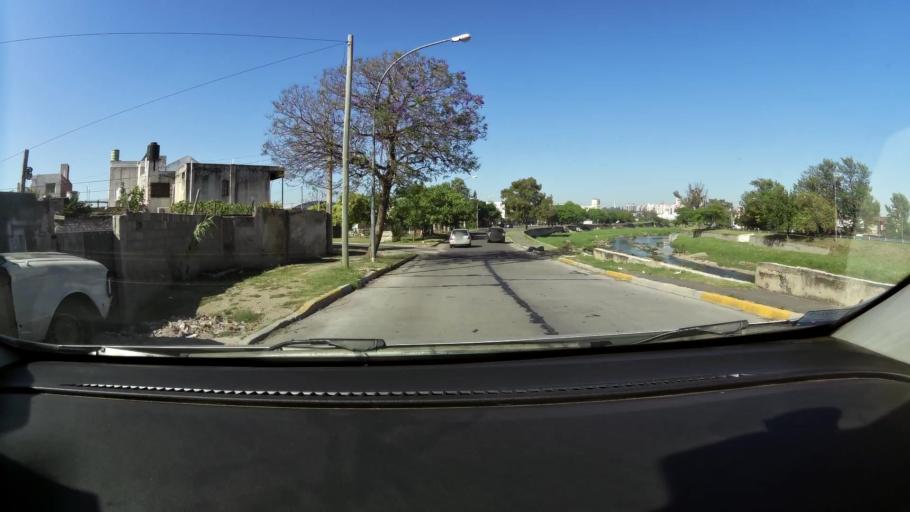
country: AR
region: Cordoba
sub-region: Departamento de Capital
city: Cordoba
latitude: -31.4216
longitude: -64.1590
